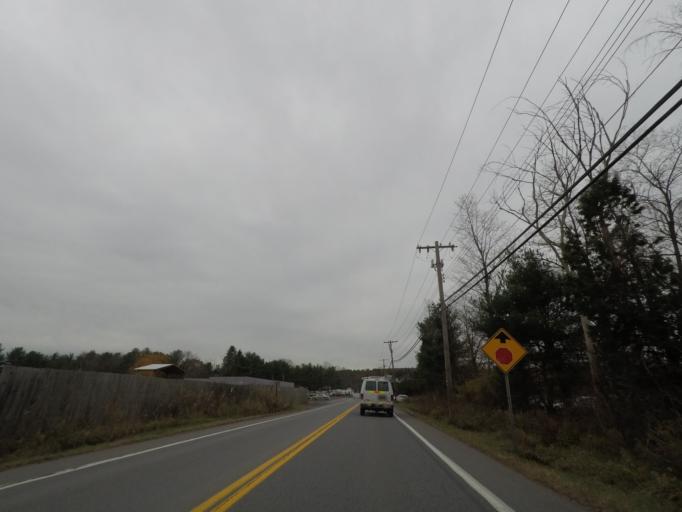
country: US
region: New York
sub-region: Schenectady County
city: East Glenville
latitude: 42.9074
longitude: -73.8716
